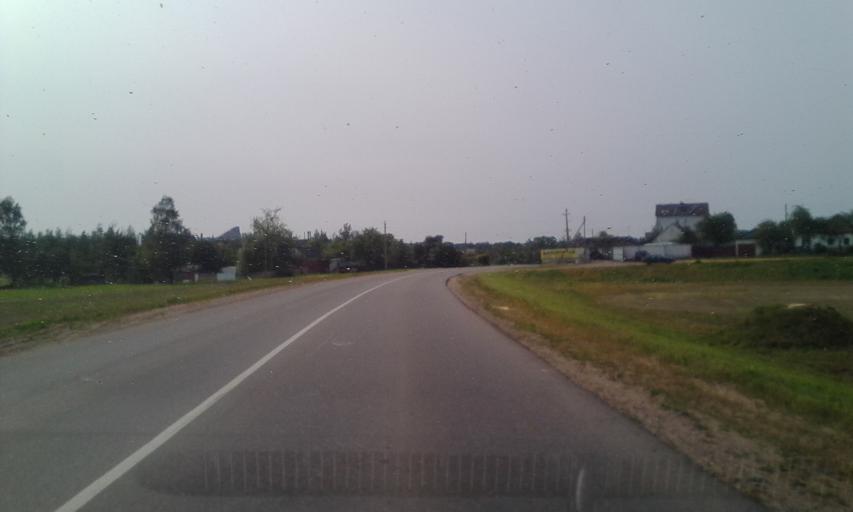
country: BY
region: Minsk
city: Hatava
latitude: 53.7795
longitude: 27.6521
